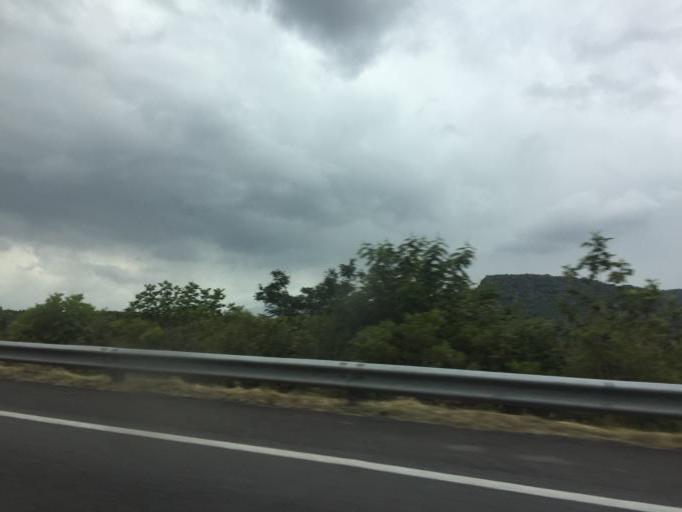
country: MX
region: Jalisco
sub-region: Zapotlan del Rey
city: Zapotlan del Rey
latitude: 20.4833
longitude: -102.9391
